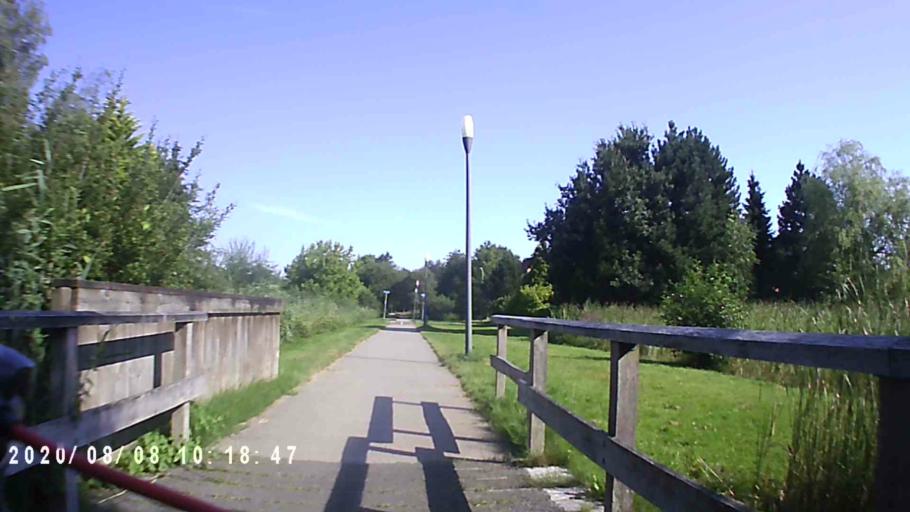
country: NL
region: Groningen
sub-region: Gemeente Leek
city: Leek
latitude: 53.1347
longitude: 6.4012
